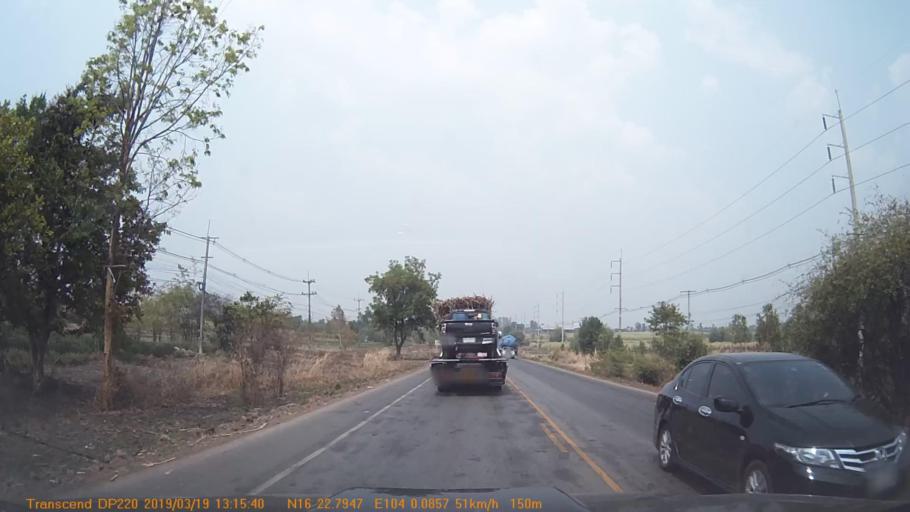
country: TH
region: Roi Et
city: Waeng
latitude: 16.3801
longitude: 104.0015
